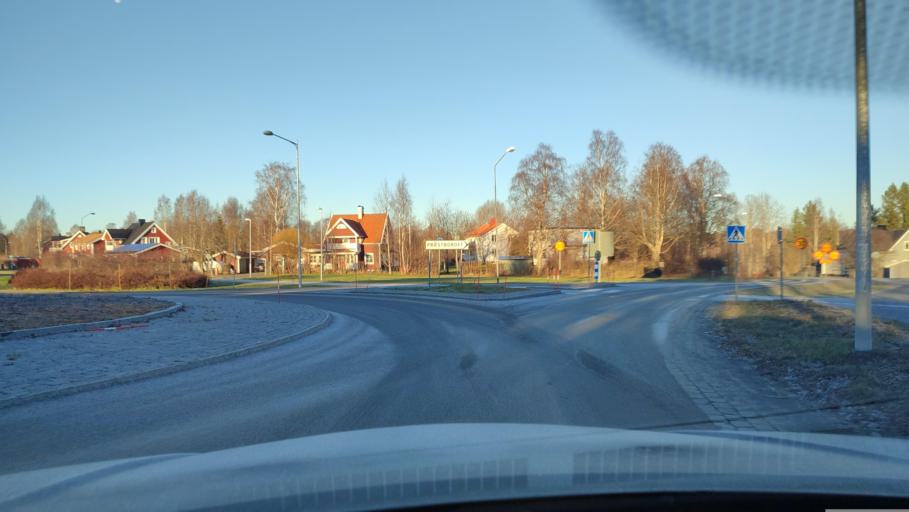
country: SE
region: Vaesterbotten
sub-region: Skelleftea Kommun
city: Viken
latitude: 64.7471
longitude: 20.9139
